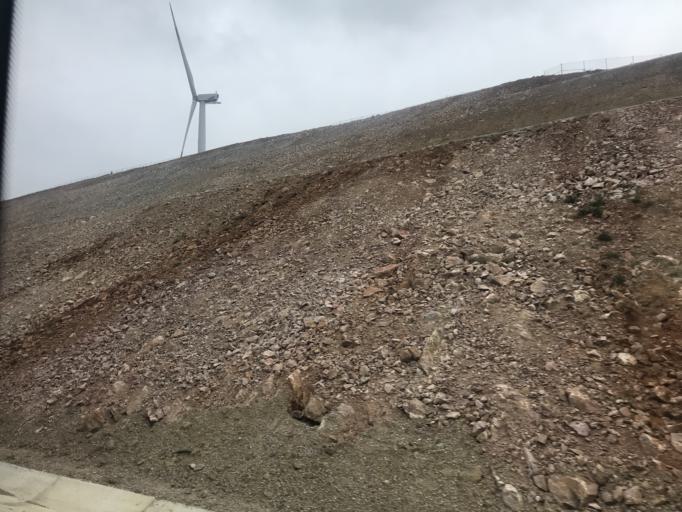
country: TR
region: Balikesir
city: Yenikoy
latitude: 39.7946
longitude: 28.0343
